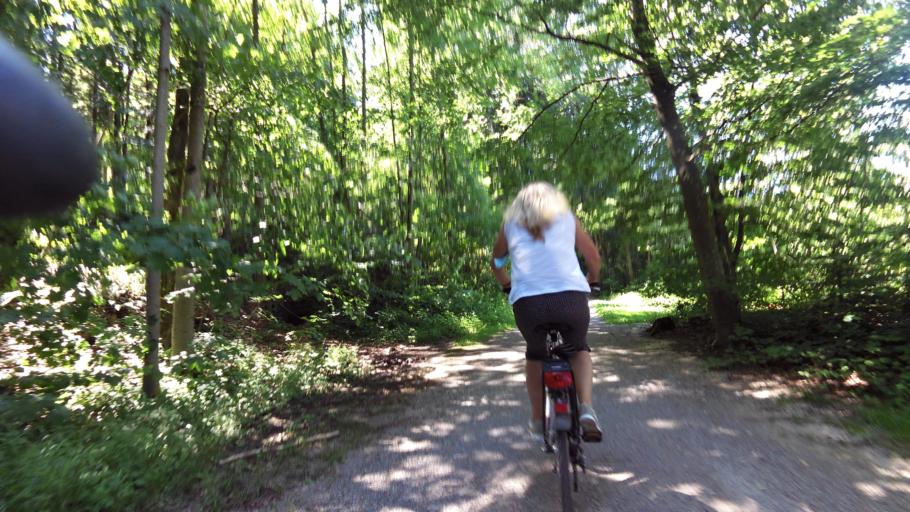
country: DE
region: Bavaria
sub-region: Upper Bavaria
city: Bad Wiessee
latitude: 47.7230
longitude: 11.7217
